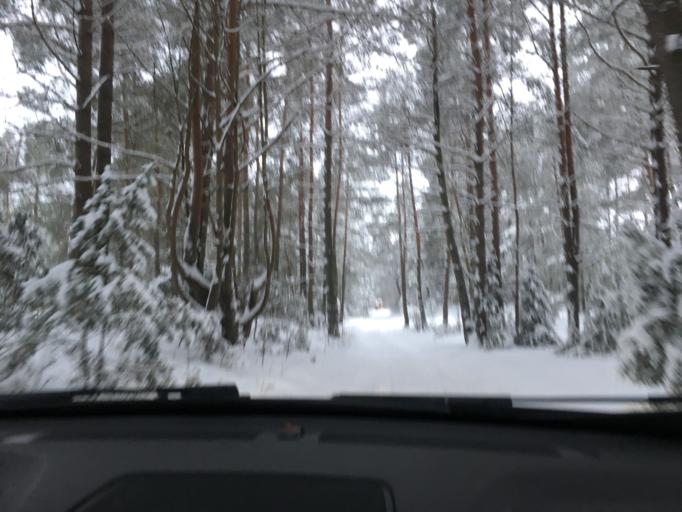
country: LT
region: Alytaus apskritis
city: Druskininkai
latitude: 53.9220
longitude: 24.1900
